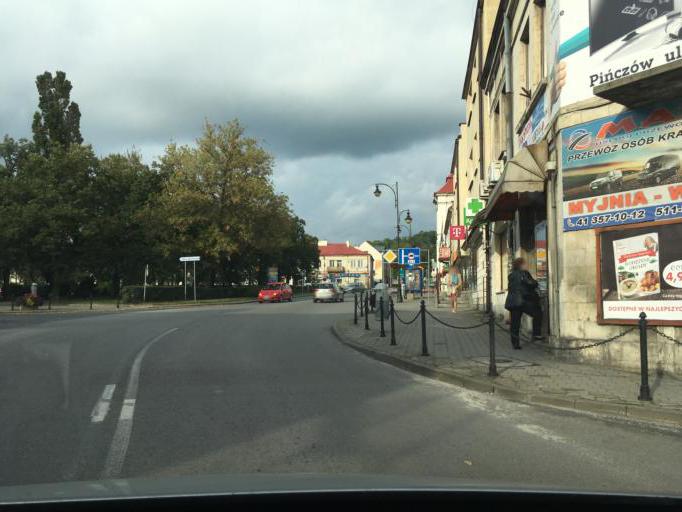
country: PL
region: Swietokrzyskie
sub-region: Powiat pinczowski
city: Pinczow
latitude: 50.5196
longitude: 20.5257
